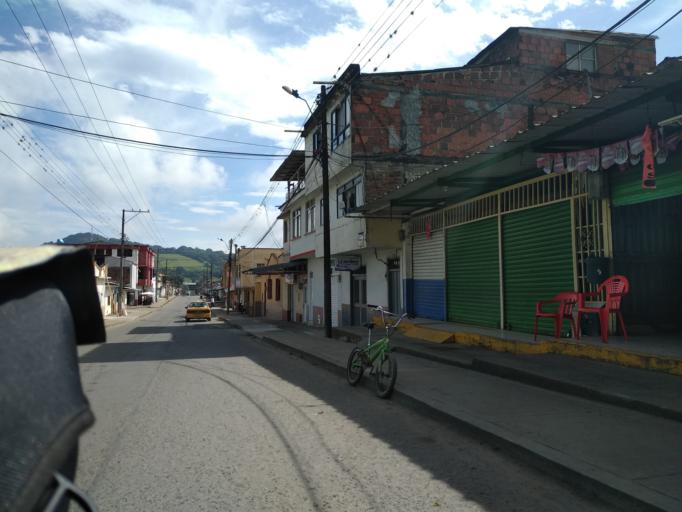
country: CO
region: Valle del Cauca
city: Caicedonia
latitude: 4.3356
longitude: -75.8286
